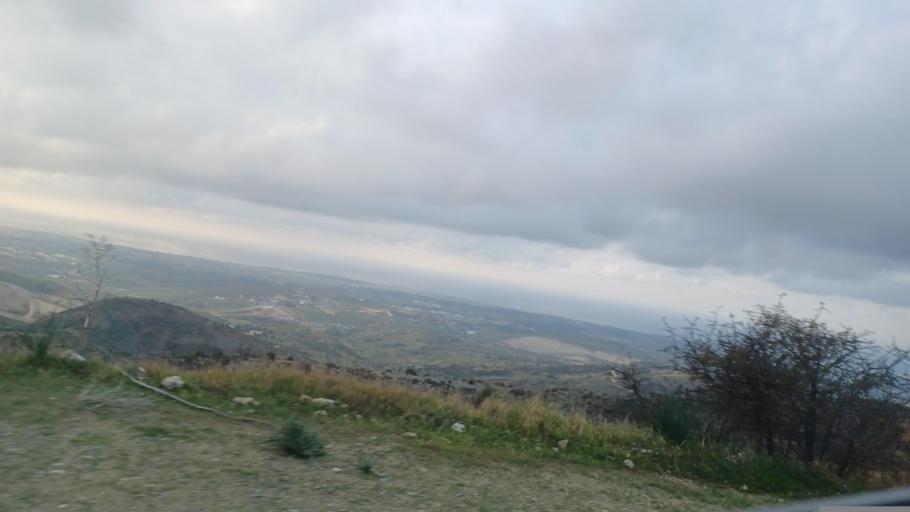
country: CY
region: Pafos
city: Mesogi
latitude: 34.7823
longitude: 32.4996
